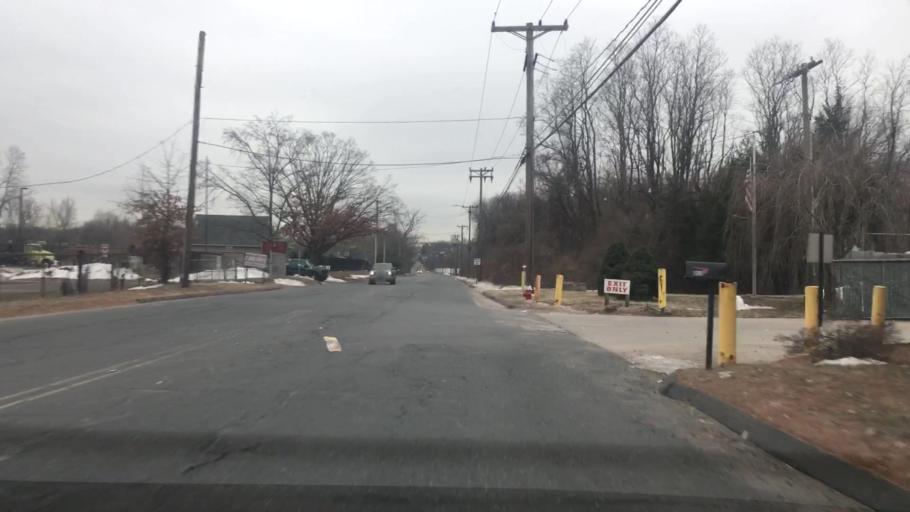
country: US
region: Connecticut
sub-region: Hartford County
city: Kensington
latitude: 41.6485
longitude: -72.7515
